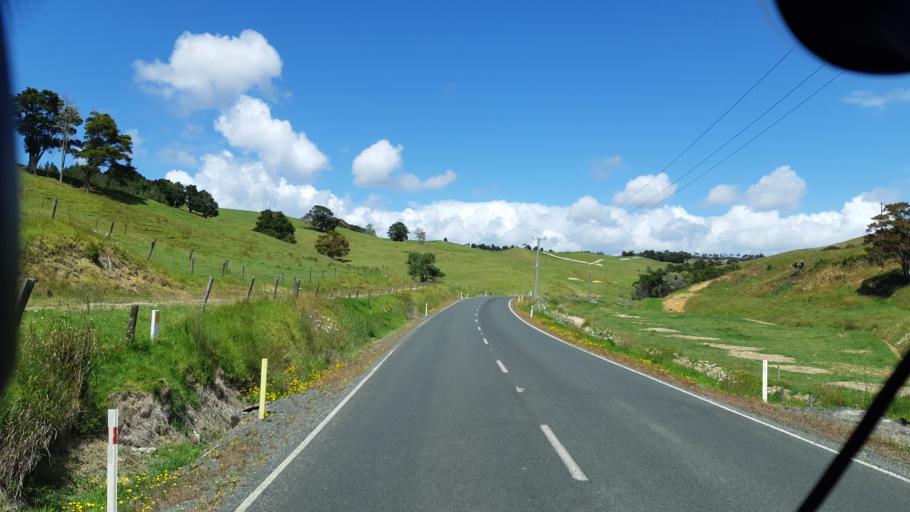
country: NZ
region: Northland
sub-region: Far North District
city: Taipa
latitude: -35.2696
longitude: 173.4910
